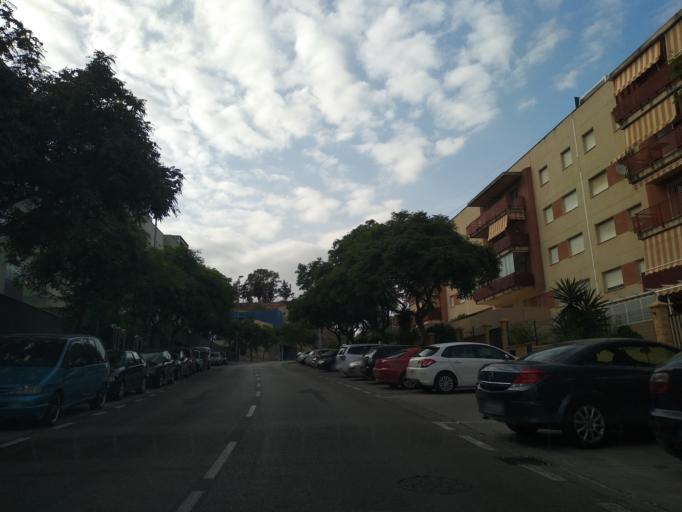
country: ES
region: Andalusia
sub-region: Provincia de Malaga
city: Malaga
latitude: 36.7317
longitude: -4.4751
